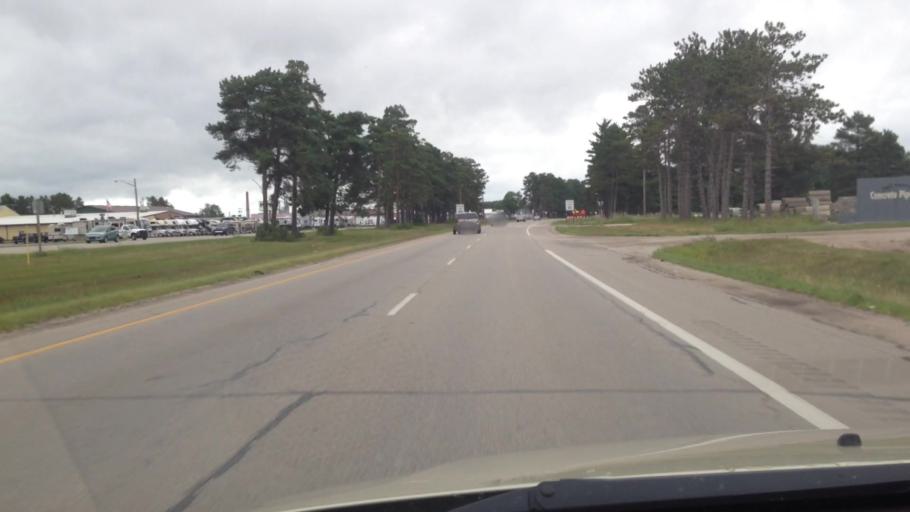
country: US
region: Michigan
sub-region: Delta County
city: Escanaba
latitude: 45.7814
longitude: -87.0829
